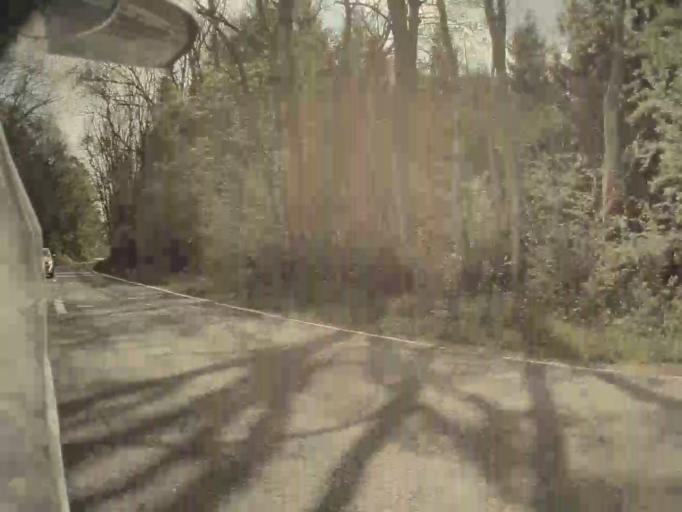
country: BE
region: Wallonia
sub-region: Province du Luxembourg
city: Tellin
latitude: 50.0746
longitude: 5.2013
